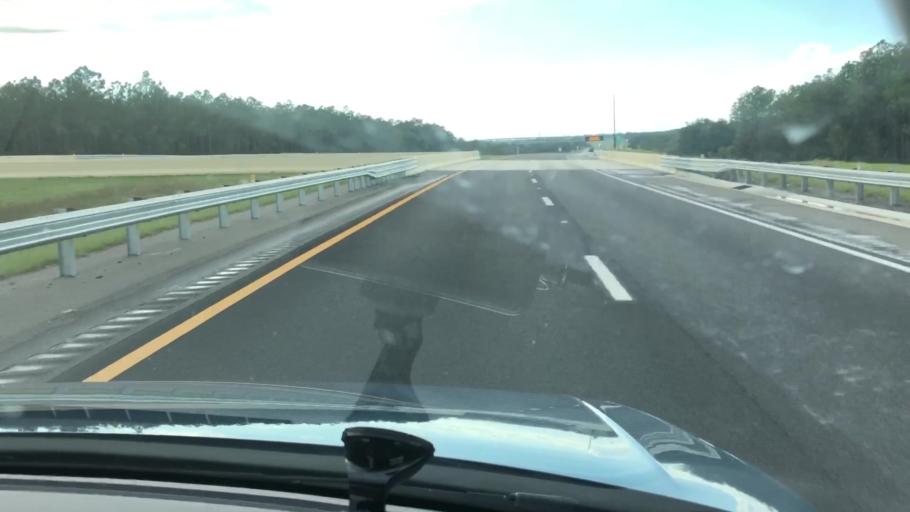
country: US
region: Florida
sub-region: Lake County
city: Mount Plymouth
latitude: 28.7761
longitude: -81.5318
